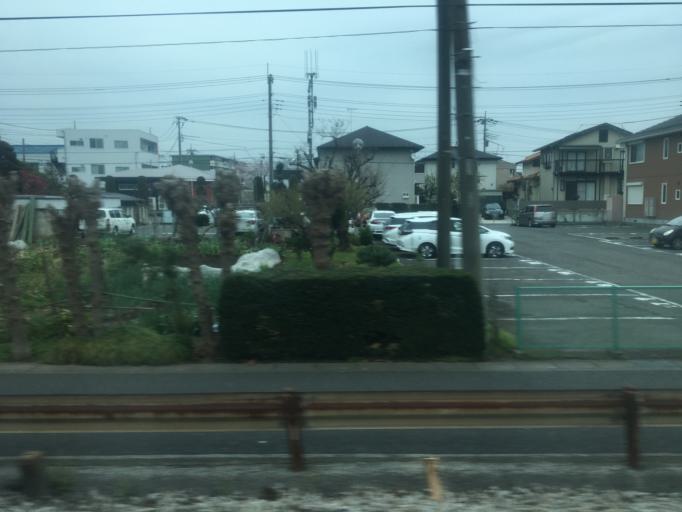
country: JP
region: Saitama
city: Ageoshimo
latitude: 35.9525
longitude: 139.6020
